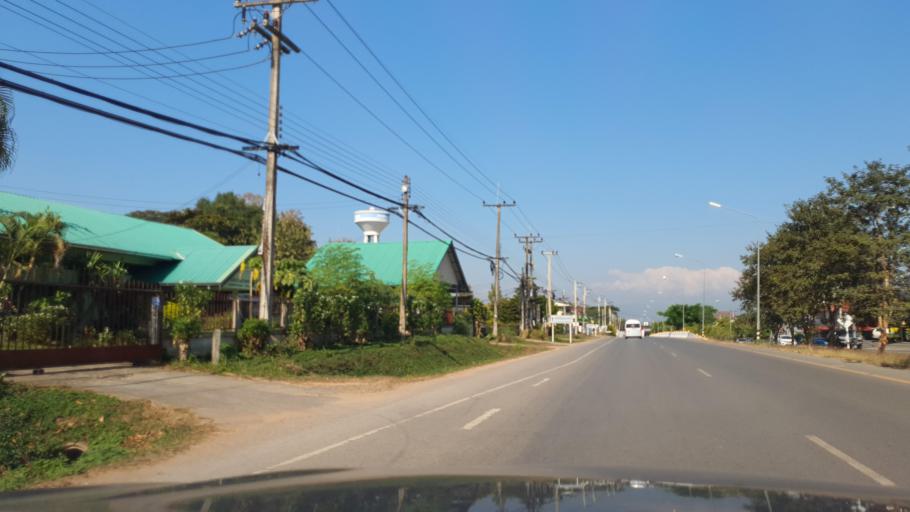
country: TH
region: Nan
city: Pua
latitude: 19.1726
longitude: 100.9190
